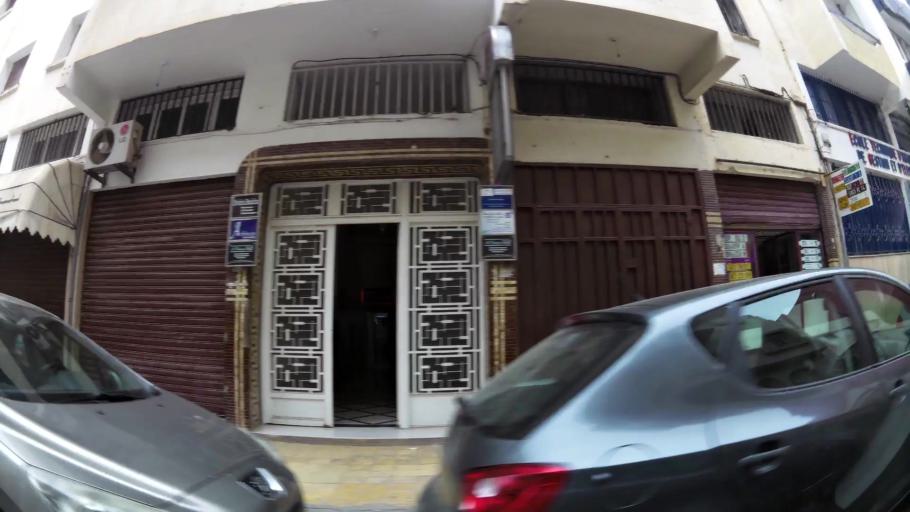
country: MA
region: Fes-Boulemane
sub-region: Fes
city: Fes
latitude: 34.0334
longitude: -4.9981
